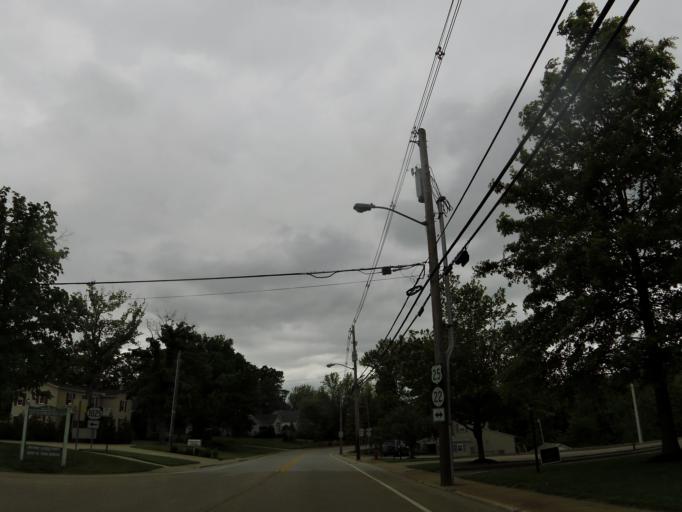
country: US
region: Kentucky
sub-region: Grant County
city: Williamstown
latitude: 38.6417
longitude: -84.5604
